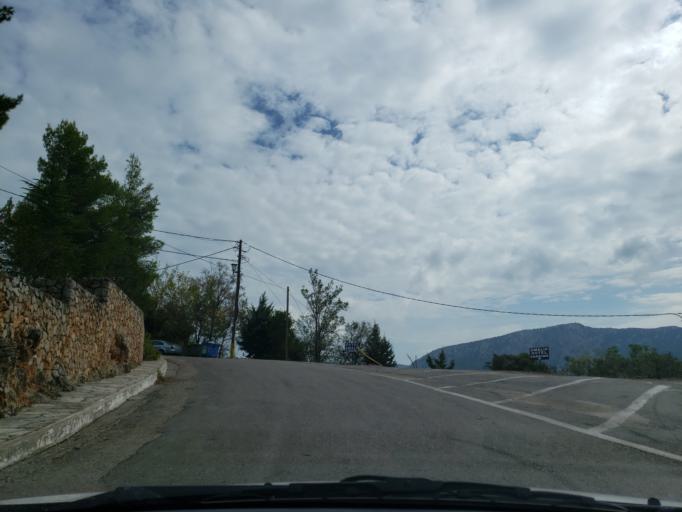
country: GR
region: Central Greece
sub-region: Nomos Fokidos
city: Delphi
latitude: 38.4809
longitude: 22.4904
